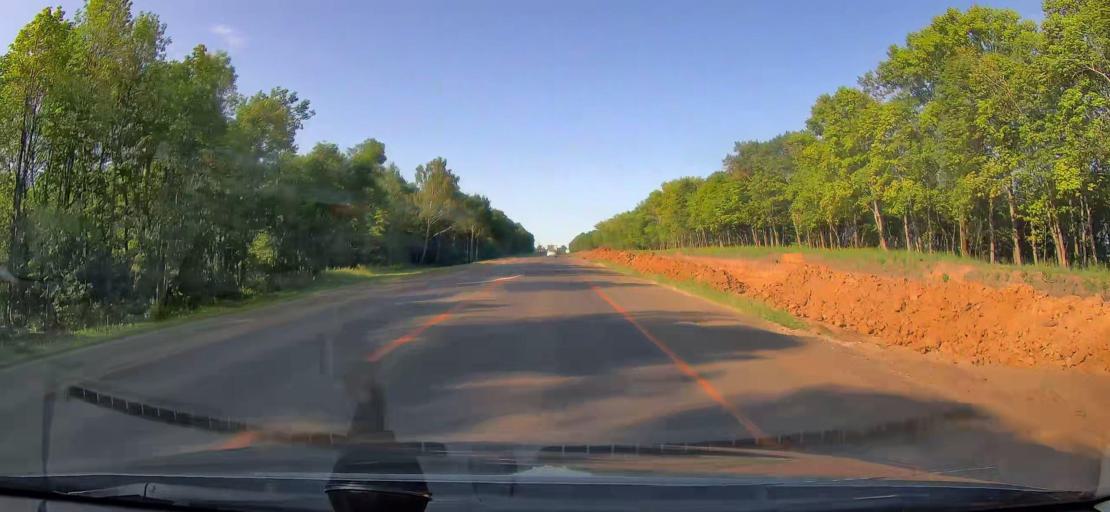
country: RU
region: Tula
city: Bol'shoye Skuratovo
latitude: 53.4085
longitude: 36.7730
